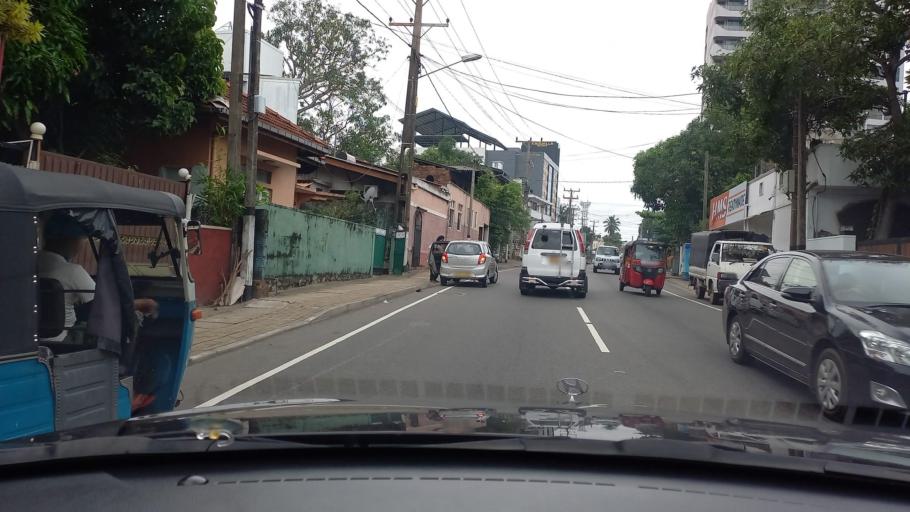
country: LK
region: Western
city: Sri Jayewardenepura Kotte
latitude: 6.8781
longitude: 79.9001
